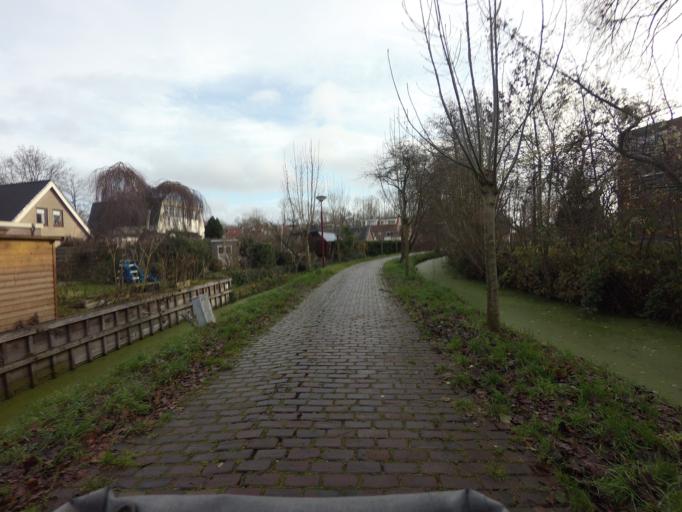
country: NL
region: Utrecht
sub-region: Gemeente Nieuwegein
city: Nieuwegein
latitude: 52.0236
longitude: 5.0808
